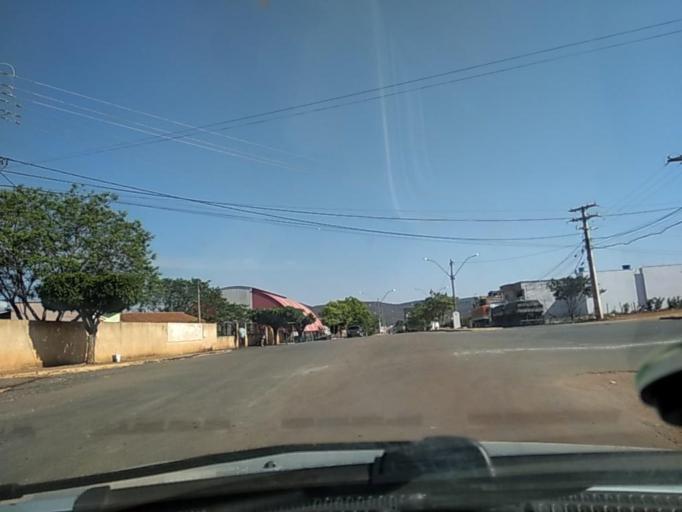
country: BR
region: Bahia
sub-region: Caetite
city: Caetite
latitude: -14.0534
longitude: -42.4845
